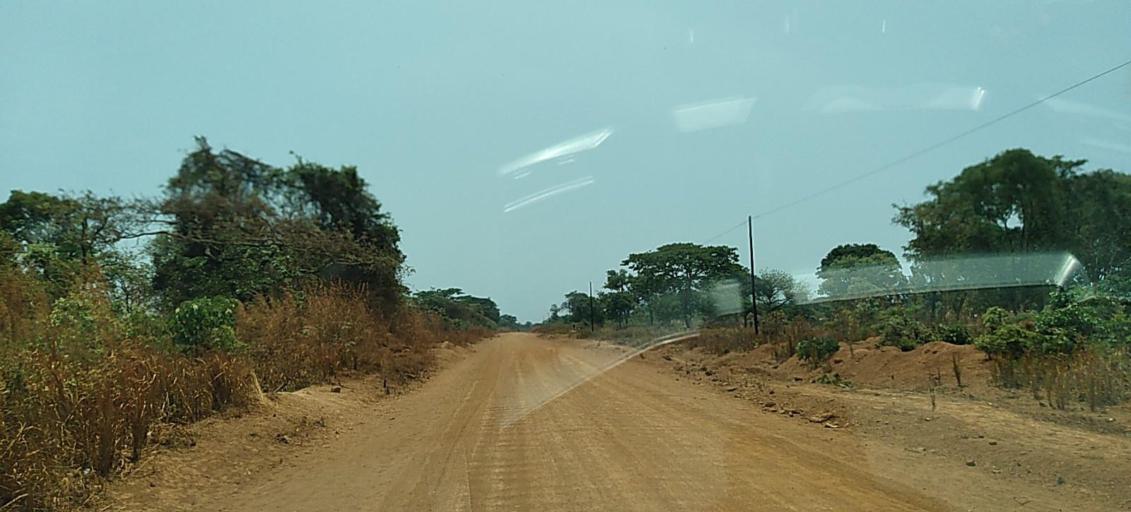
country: CD
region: Katanga
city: Kipushi
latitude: -11.9339
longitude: 26.9715
